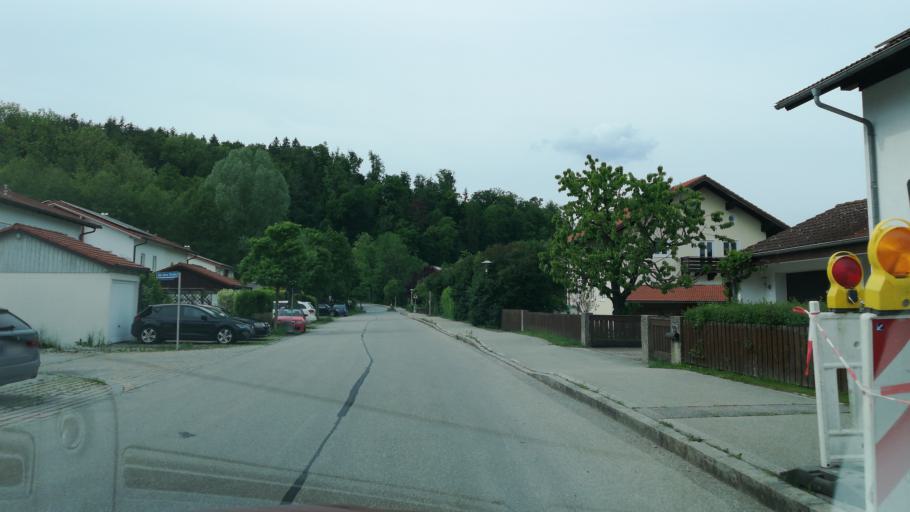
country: DE
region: Bavaria
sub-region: Upper Bavaria
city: Mehring
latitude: 48.1368
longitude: 12.7905
